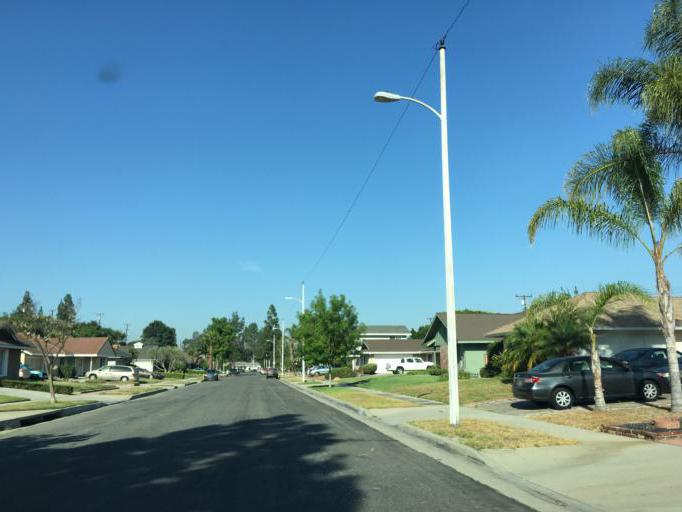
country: US
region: California
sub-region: Los Angeles County
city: Avocado Heights
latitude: 34.0415
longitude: -118.0054
